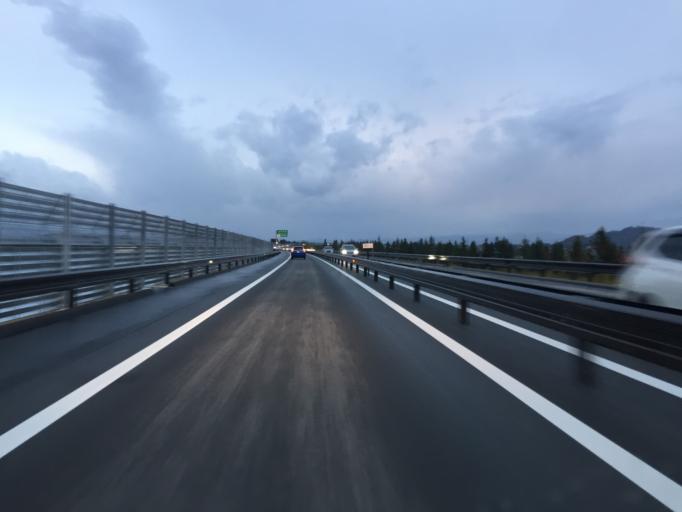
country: JP
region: Yamagata
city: Yonezawa
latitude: 37.9118
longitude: 140.1406
